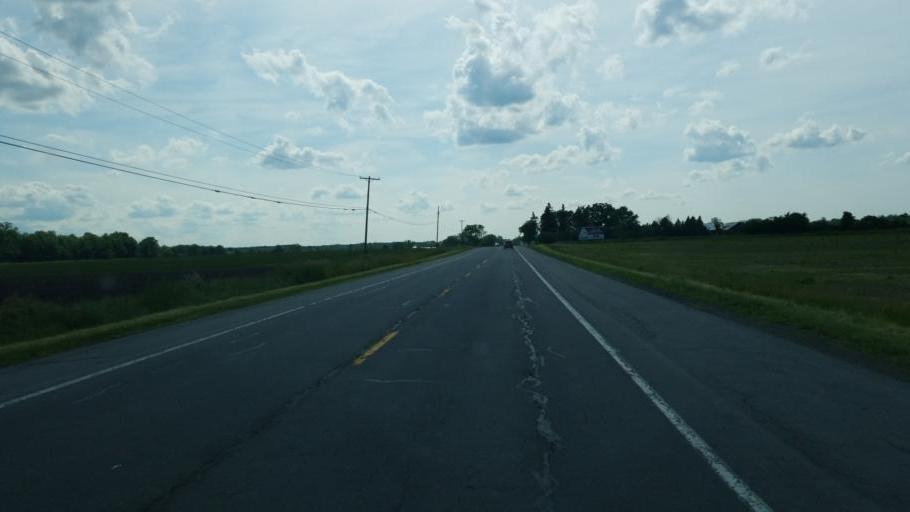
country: US
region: New York
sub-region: Ontario County
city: Clifton Springs
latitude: 42.8610
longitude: -77.1285
